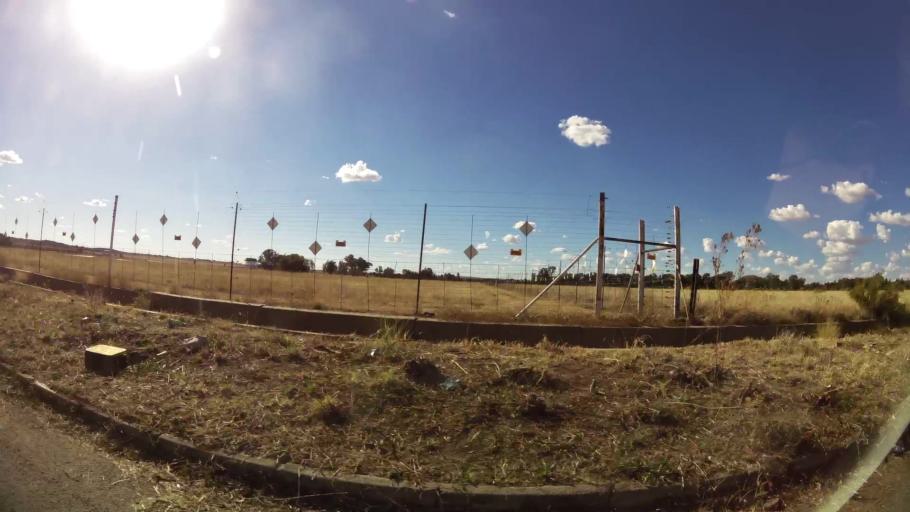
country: ZA
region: North-West
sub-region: Dr Kenneth Kaunda District Municipality
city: Klerksdorp
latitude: -26.8174
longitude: 26.6580
